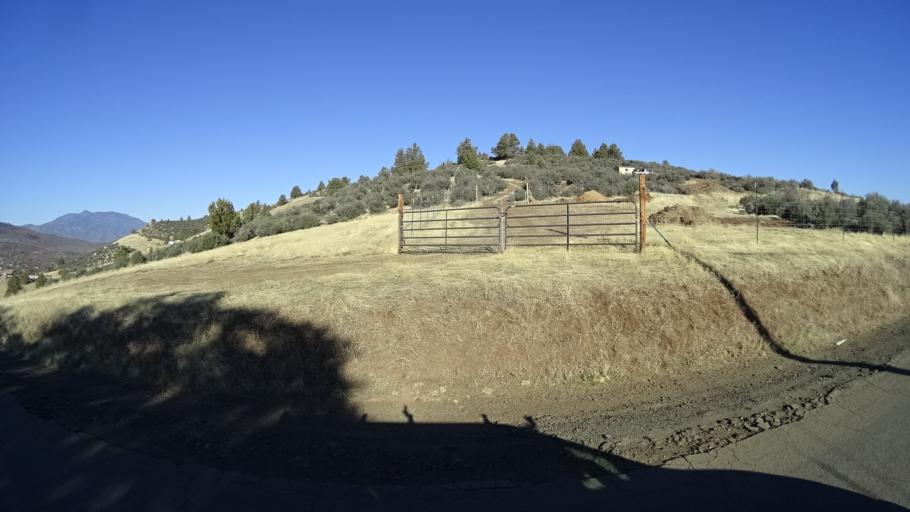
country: US
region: California
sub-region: Siskiyou County
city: Montague
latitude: 41.8795
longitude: -122.4582
